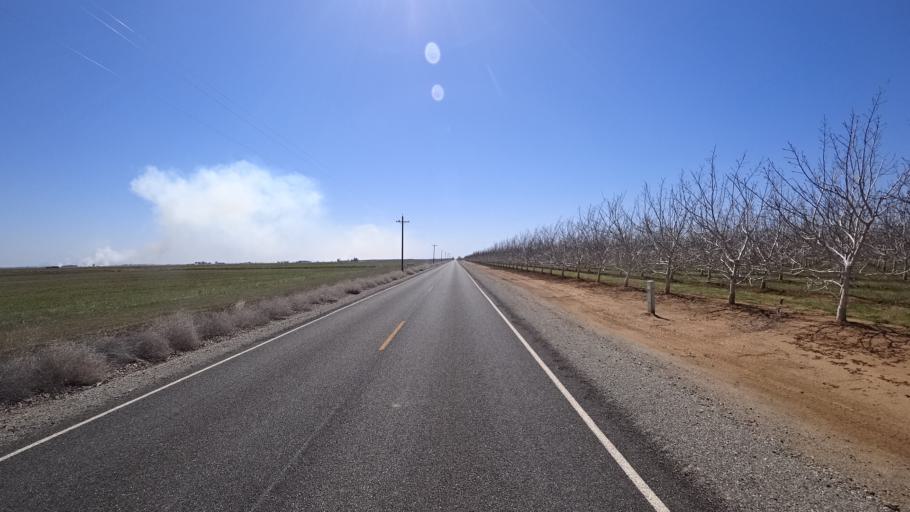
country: US
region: California
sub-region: Glenn County
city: Willows
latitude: 39.4776
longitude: -122.2490
